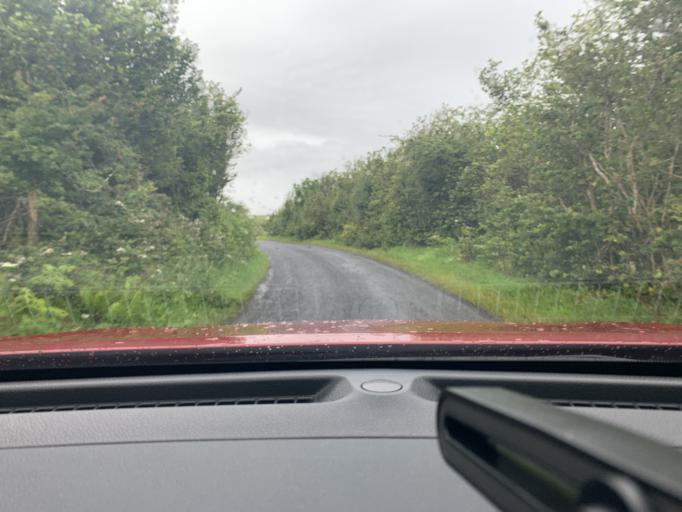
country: GB
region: Northern Ireland
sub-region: Fermanagh District
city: Enniskillen
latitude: 54.2546
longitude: -7.8310
